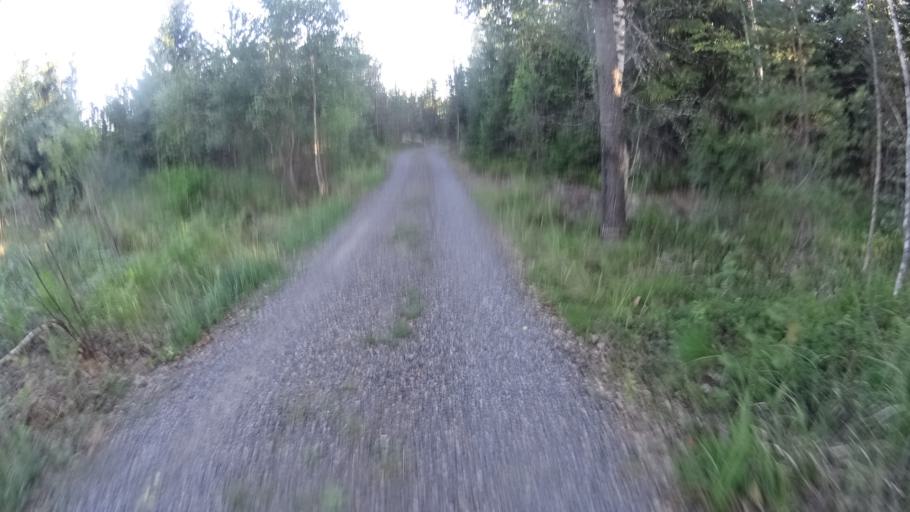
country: FI
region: Uusimaa
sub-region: Helsinki
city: Karkkila
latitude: 60.5938
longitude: 24.1050
